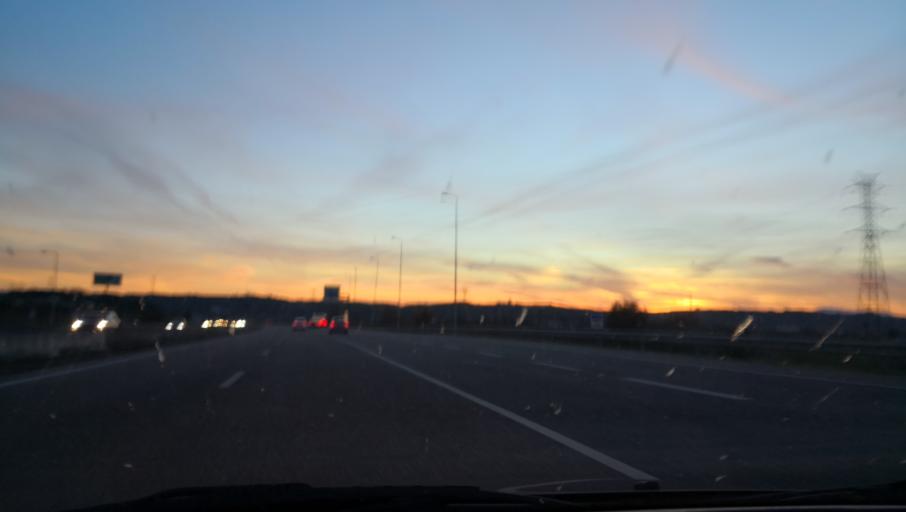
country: PT
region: Santarem
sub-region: Santarem
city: Santarem
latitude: 39.2607
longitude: -8.7330
